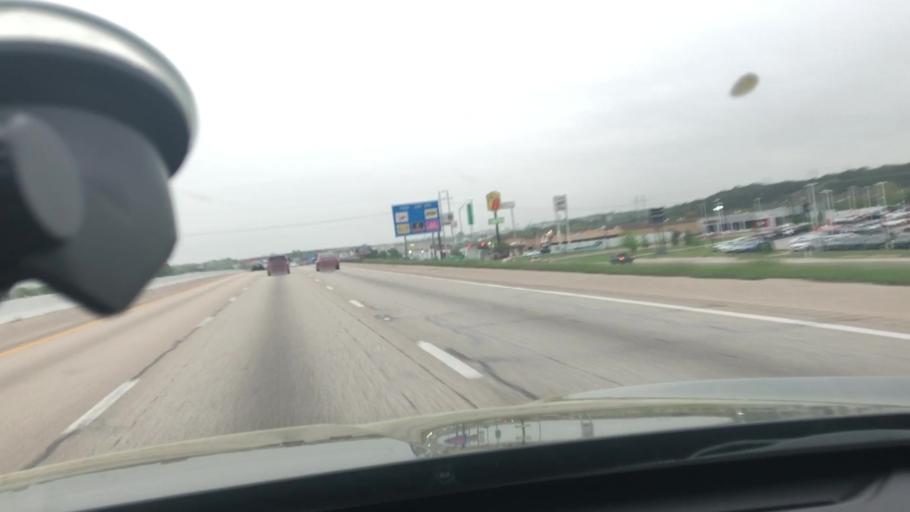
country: US
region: Texas
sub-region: Bell County
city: Belton
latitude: 31.0789
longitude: -97.4139
